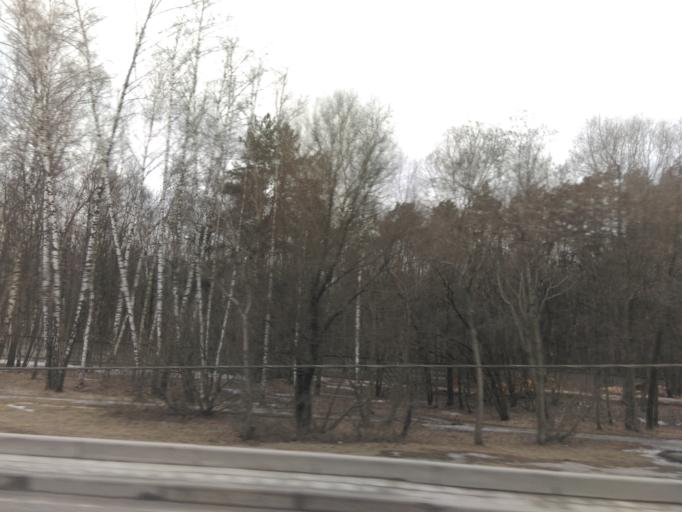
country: RU
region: Moskovskaya
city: Bol'shaya Setun'
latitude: 55.7564
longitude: 37.3979
